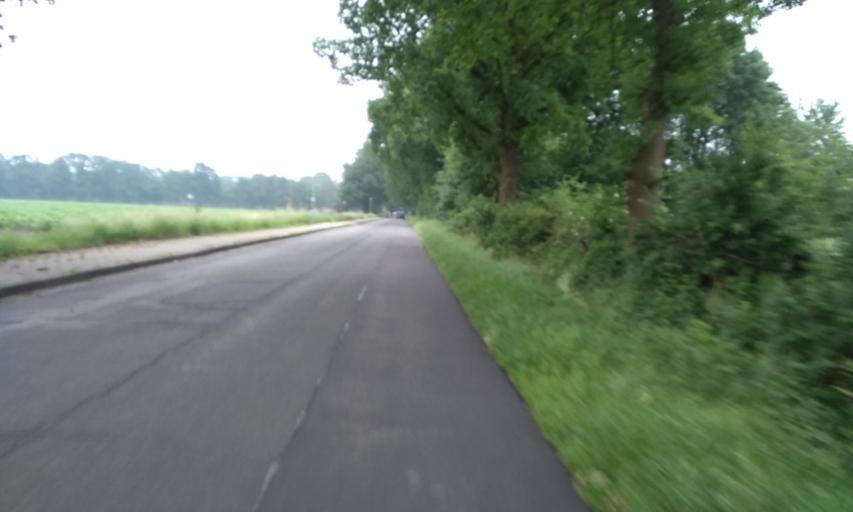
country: DE
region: Lower Saxony
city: Deinste
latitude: 53.5477
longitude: 9.4662
